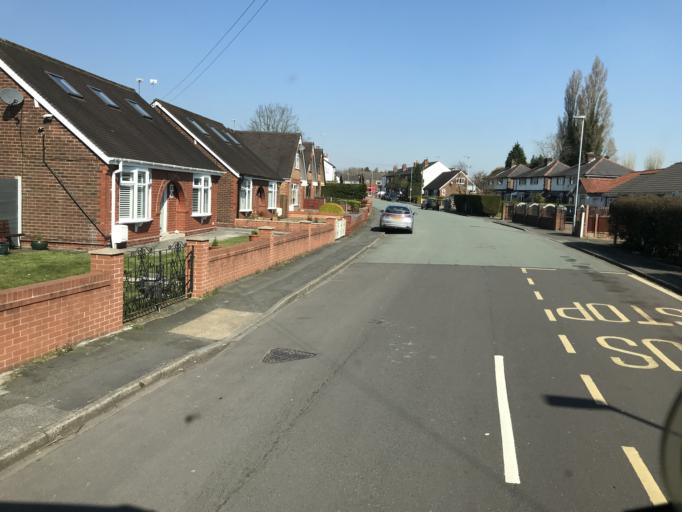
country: GB
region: England
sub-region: Trafford
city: Partington
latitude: 53.4133
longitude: -2.4567
